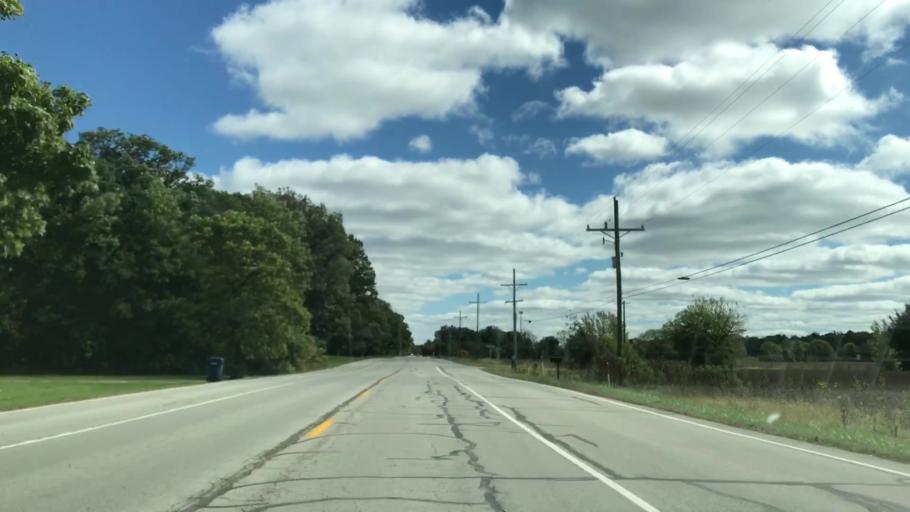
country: US
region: Indiana
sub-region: Hamilton County
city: Westfield
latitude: 40.0867
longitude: -86.1102
